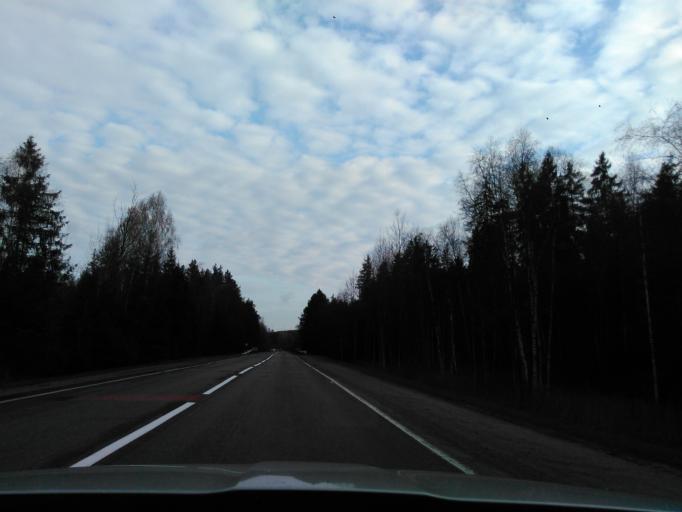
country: BY
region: Minsk
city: Plyeshchanitsy
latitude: 54.3893
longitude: 27.8719
